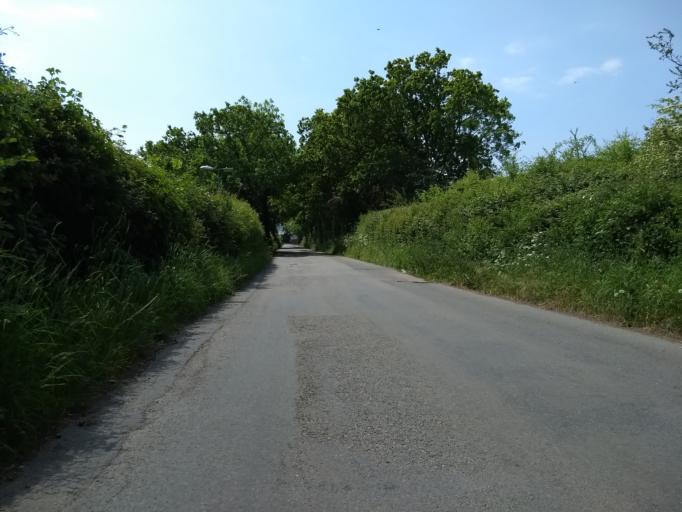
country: GB
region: England
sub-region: Isle of Wight
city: East Cowes
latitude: 50.7350
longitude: -1.2740
